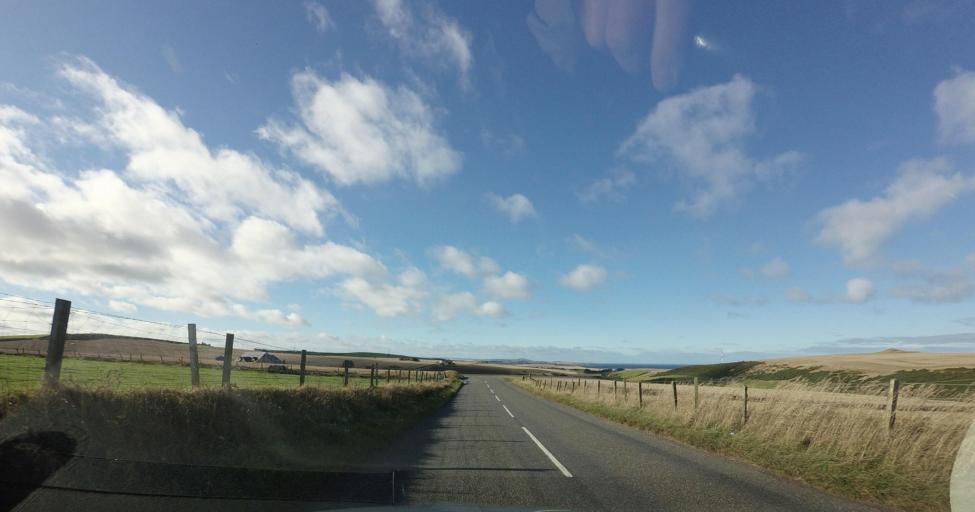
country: GB
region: Scotland
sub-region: Aberdeenshire
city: Macduff
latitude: 57.6642
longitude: -2.4029
